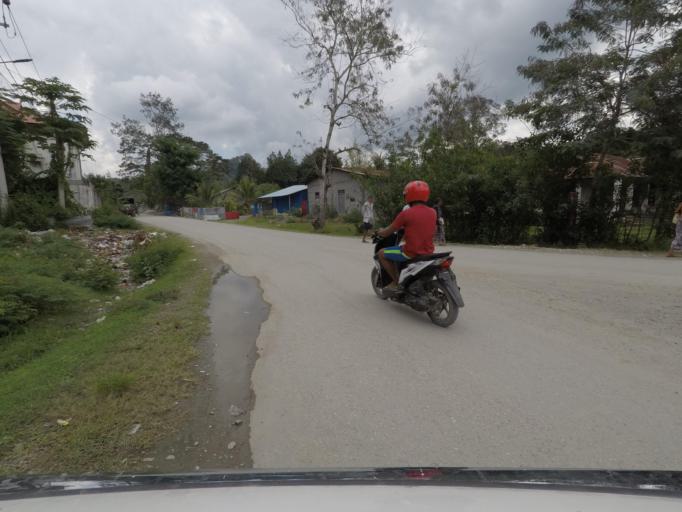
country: TL
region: Viqueque
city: Viqueque
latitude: -8.8696
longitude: 126.3667
